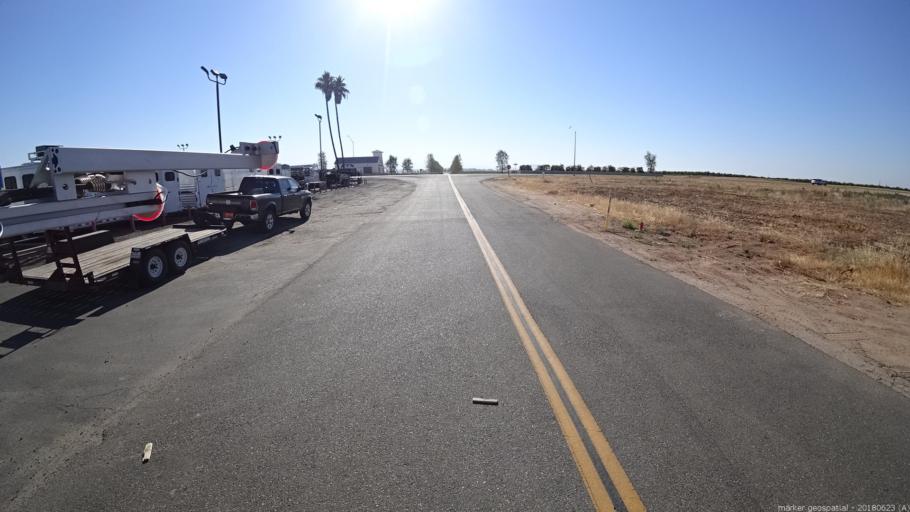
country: US
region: California
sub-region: Madera County
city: Bonadelle Ranchos-Madera Ranchos
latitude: 36.9595
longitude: -119.7950
